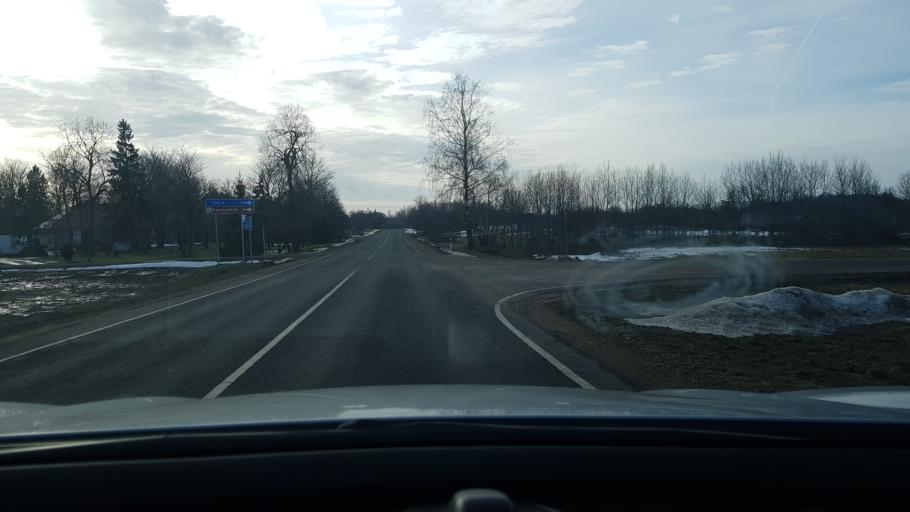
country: EE
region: Saare
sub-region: Kuressaare linn
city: Kuressaare
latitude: 58.3096
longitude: 22.5419
